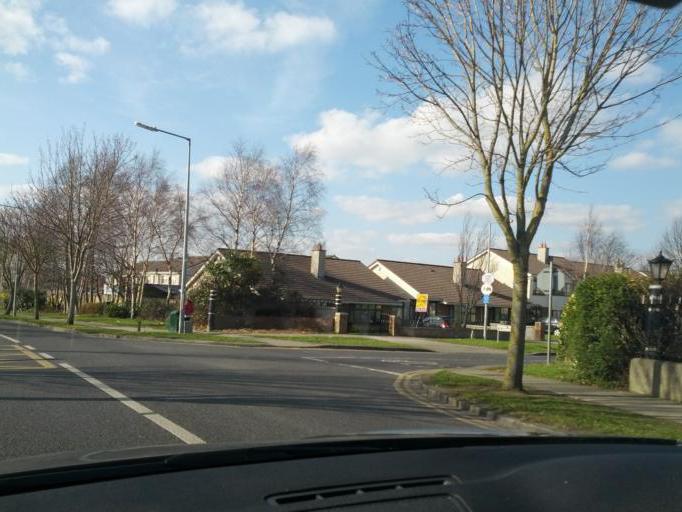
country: IE
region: Leinster
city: Lucan
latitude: 53.3462
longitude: -6.4207
